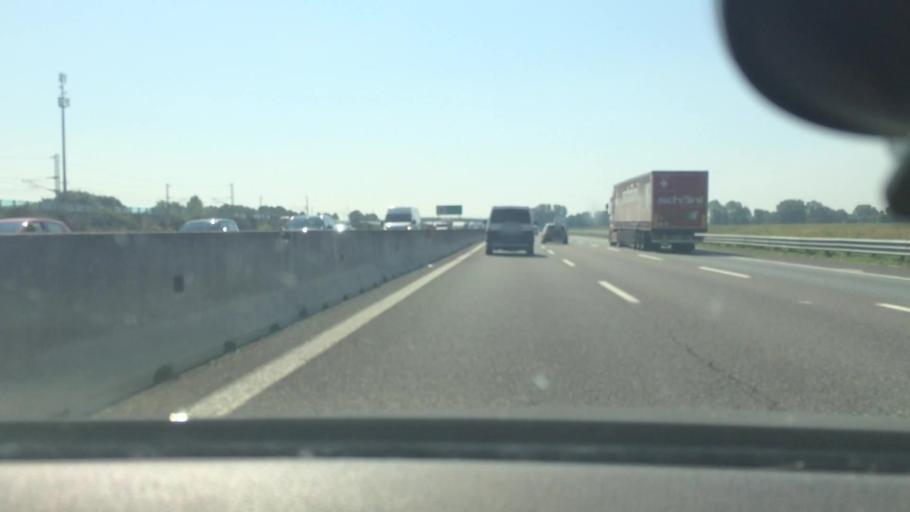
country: IT
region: Lombardy
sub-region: Provincia di Lodi
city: Lodi Vecchio
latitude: 45.2979
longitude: 9.4112
